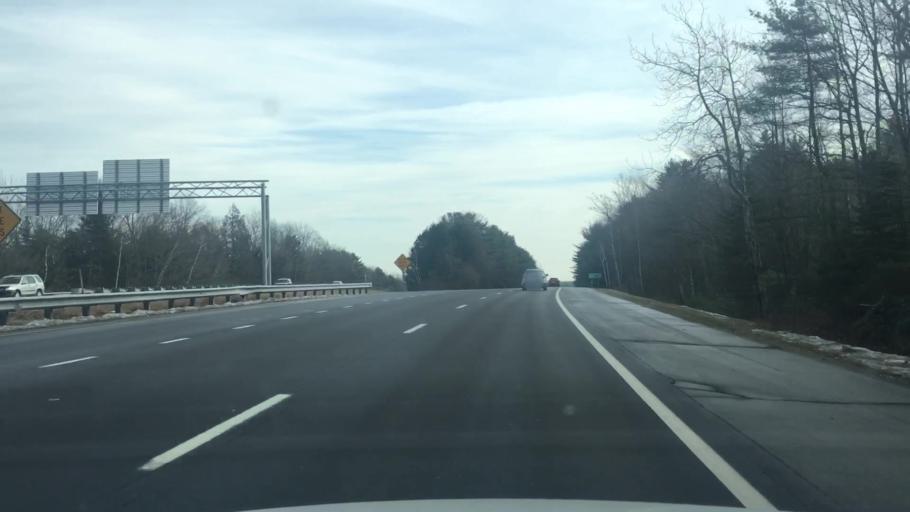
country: US
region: Maine
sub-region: Sagadahoc County
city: Topsham
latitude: 43.9163
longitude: -70.0137
